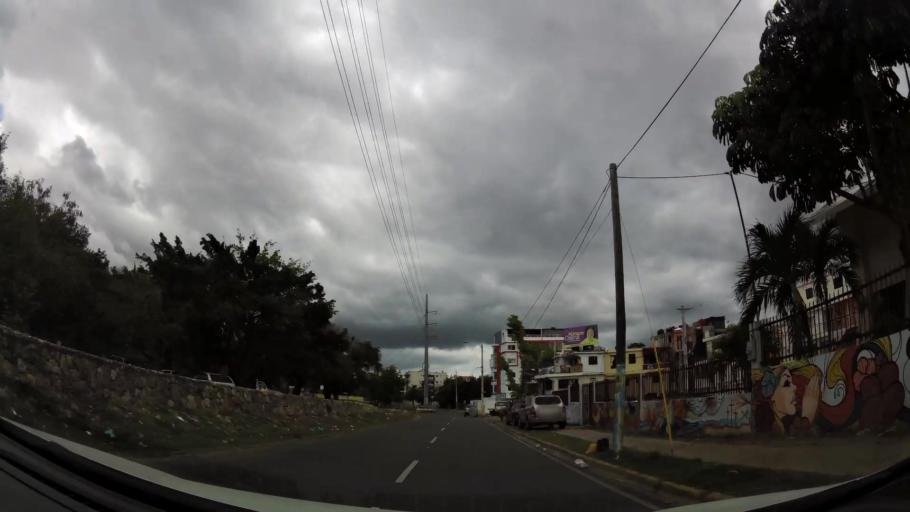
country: DO
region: Nacional
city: Bella Vista
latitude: 18.4425
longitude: -69.9516
